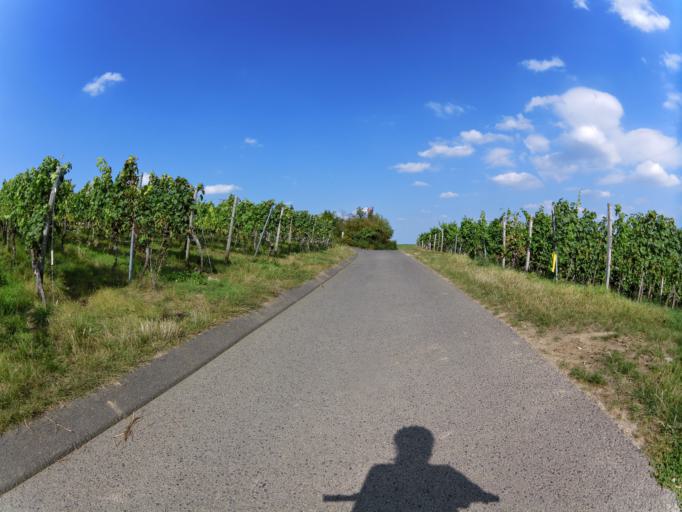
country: DE
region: Bavaria
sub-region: Regierungsbezirk Unterfranken
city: Sommerach
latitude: 49.8347
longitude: 10.1731
